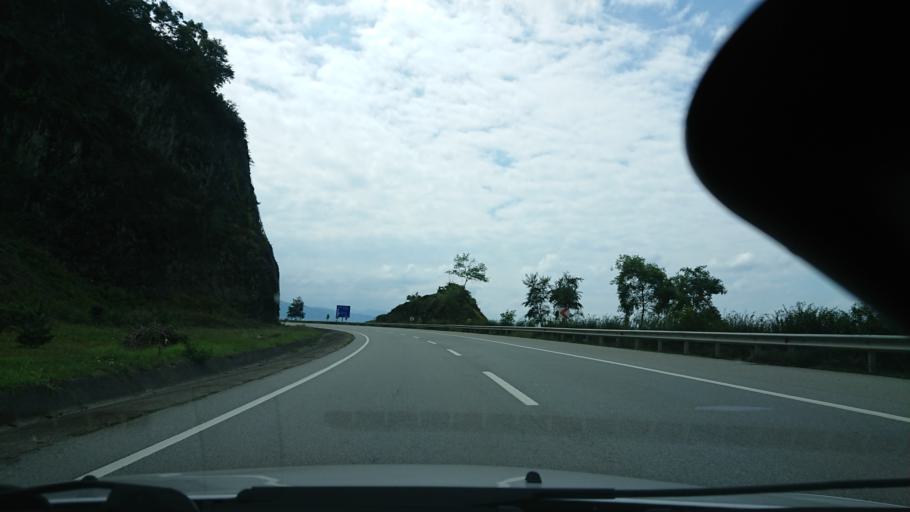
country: TR
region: Giresun
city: Kesap
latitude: 40.9432
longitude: 38.5814
